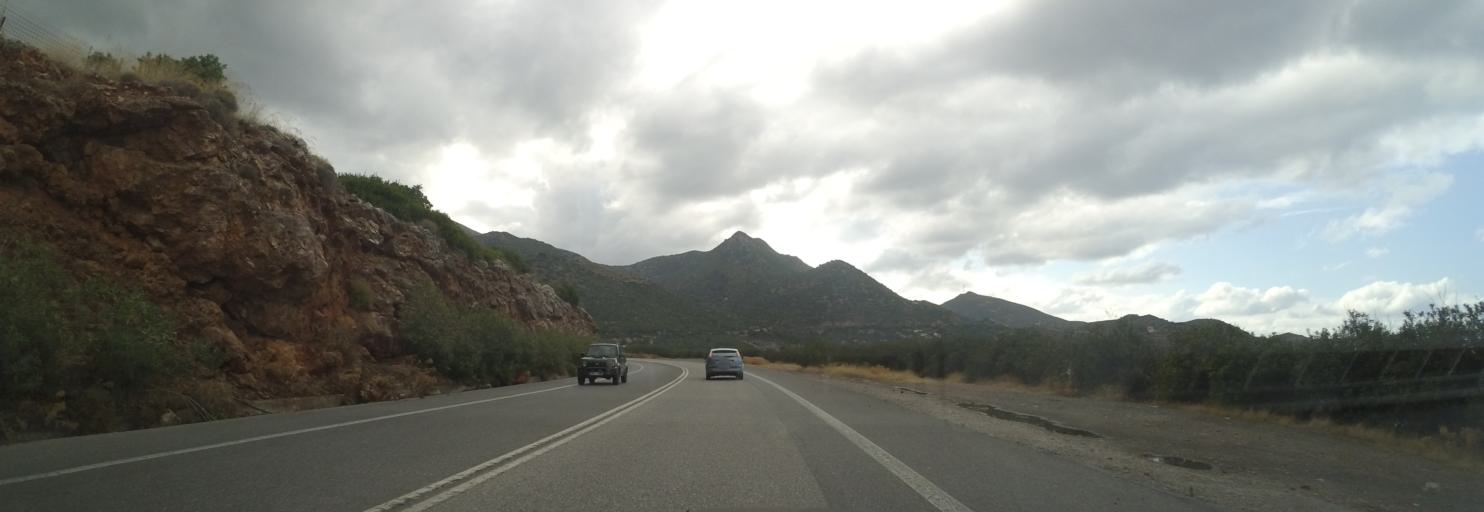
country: GR
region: Crete
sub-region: Nomos Rethymnis
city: Perama
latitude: 35.4066
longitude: 24.7912
